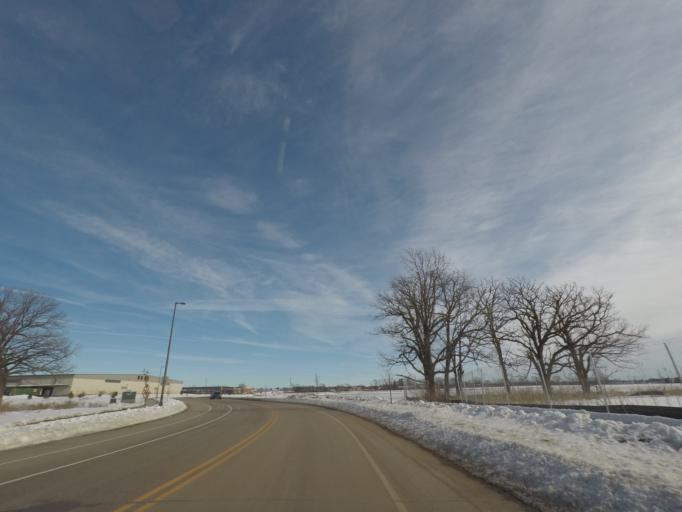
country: US
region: Wisconsin
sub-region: Dane County
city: Fitchburg
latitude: 43.0047
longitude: -89.4662
